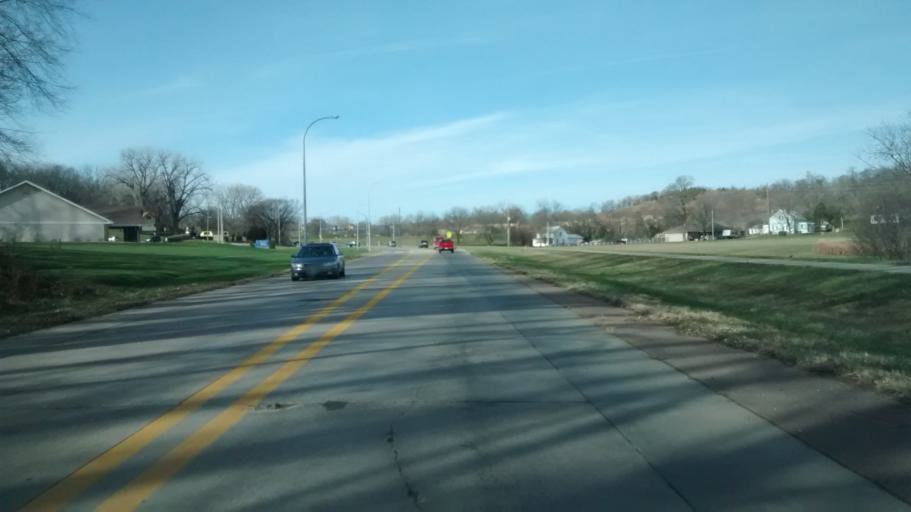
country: US
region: Iowa
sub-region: Woodbury County
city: Sioux City
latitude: 42.5391
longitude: -96.3779
